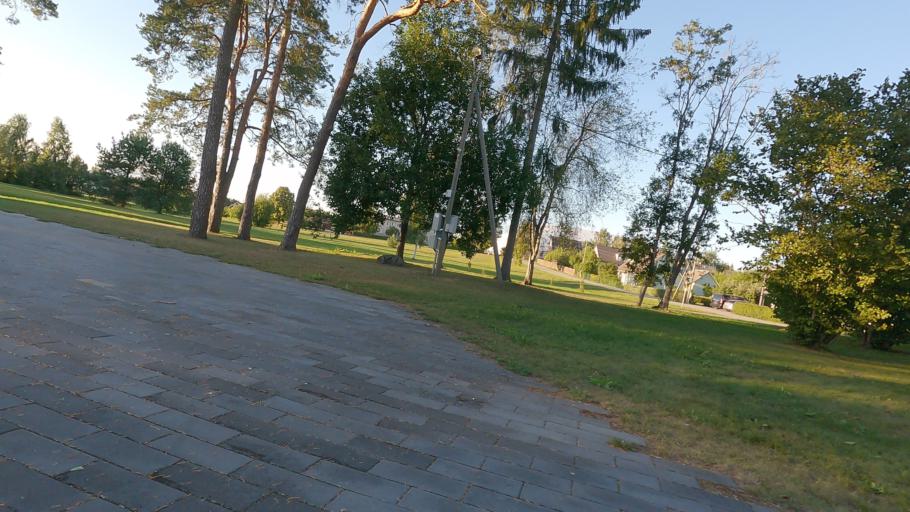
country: EE
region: Raplamaa
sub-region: Rapla vald
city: Rapla
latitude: 59.0011
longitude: 24.7835
